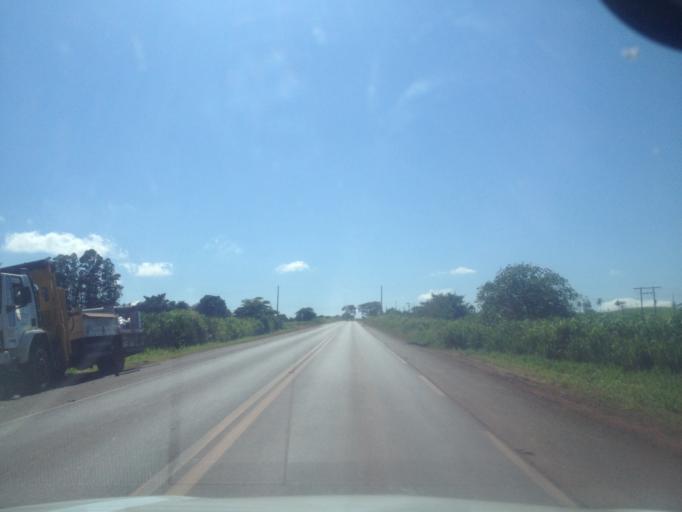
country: BR
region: Minas Gerais
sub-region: Santa Vitoria
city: Santa Vitoria
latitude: -19.0459
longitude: -50.4944
